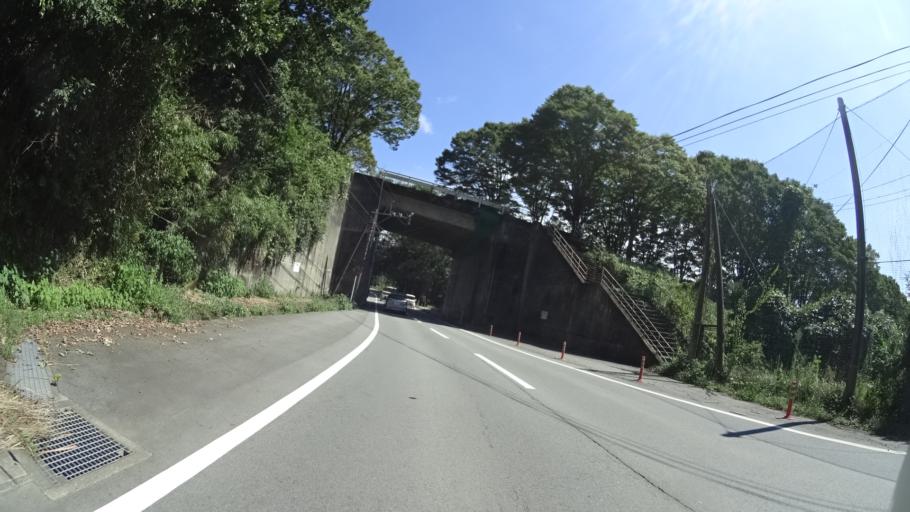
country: JP
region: Kumamoto
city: Aso
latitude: 32.8892
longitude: 130.9920
